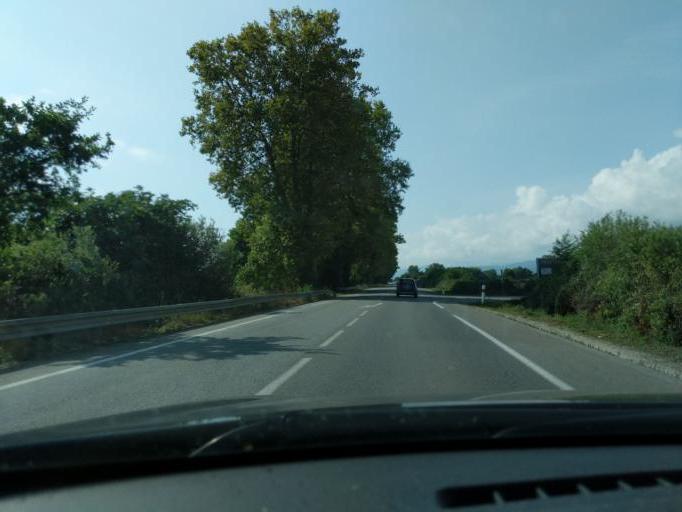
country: FR
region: Corsica
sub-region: Departement de la Haute-Corse
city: Ghisonaccia
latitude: 41.9813
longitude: 9.4002
